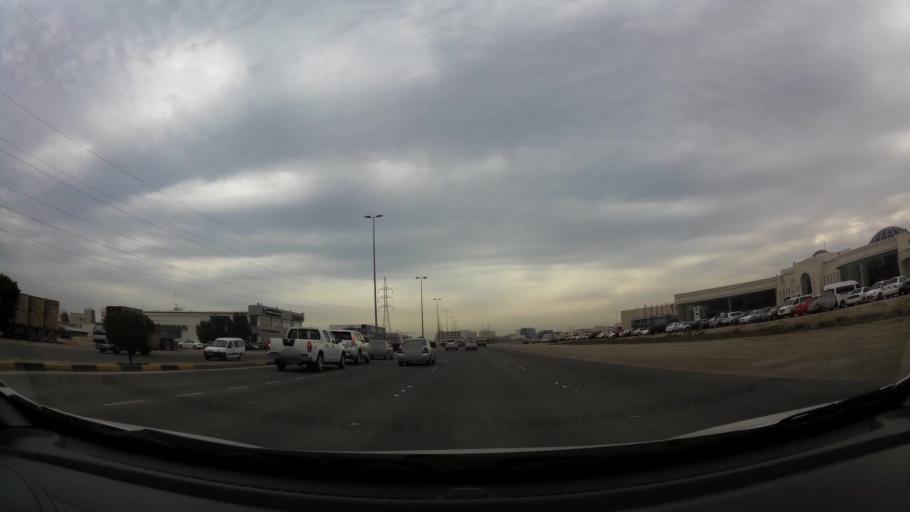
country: BH
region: Northern
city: Sitrah
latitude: 26.1550
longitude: 50.6111
